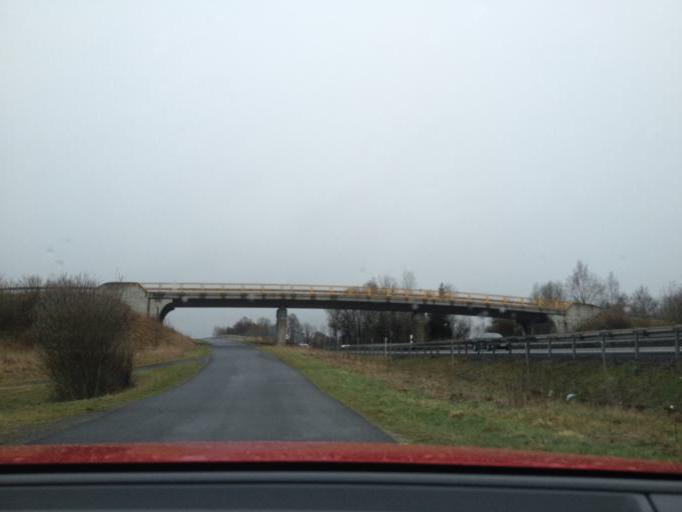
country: DE
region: Bavaria
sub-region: Upper Franconia
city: Thierstein
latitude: 50.0911
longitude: 12.0998
